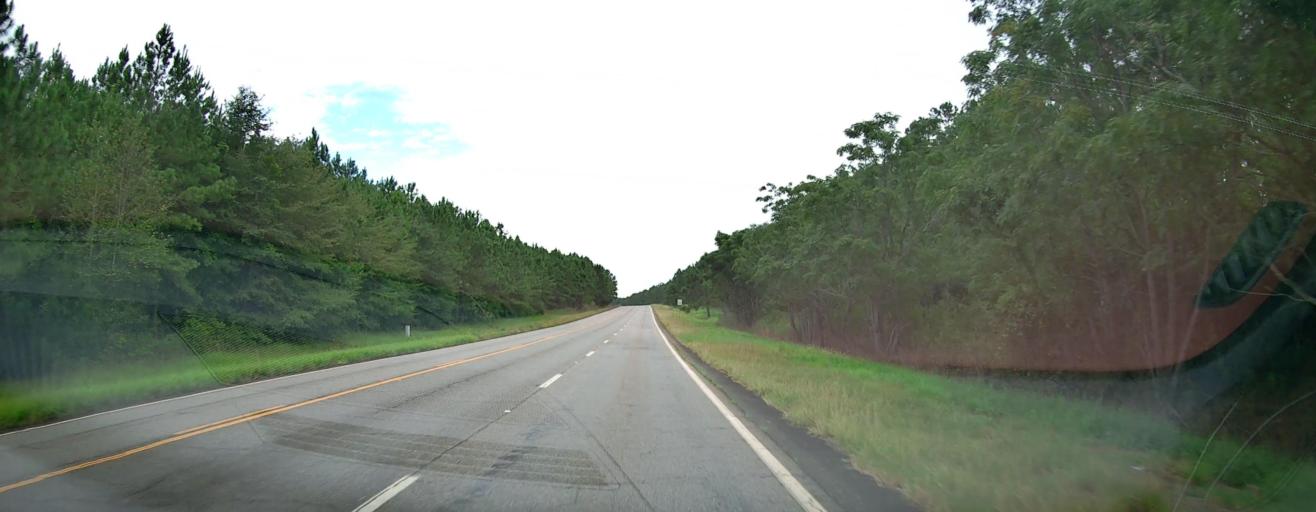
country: US
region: Georgia
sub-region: Marion County
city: Buena Vista
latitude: 32.2863
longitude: -84.4466
